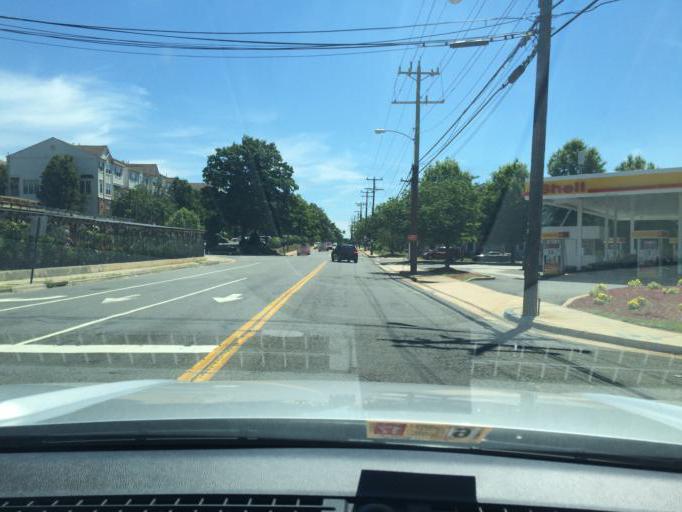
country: US
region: Virginia
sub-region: Fairfax County
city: Huntington
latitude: 38.8268
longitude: -77.0871
